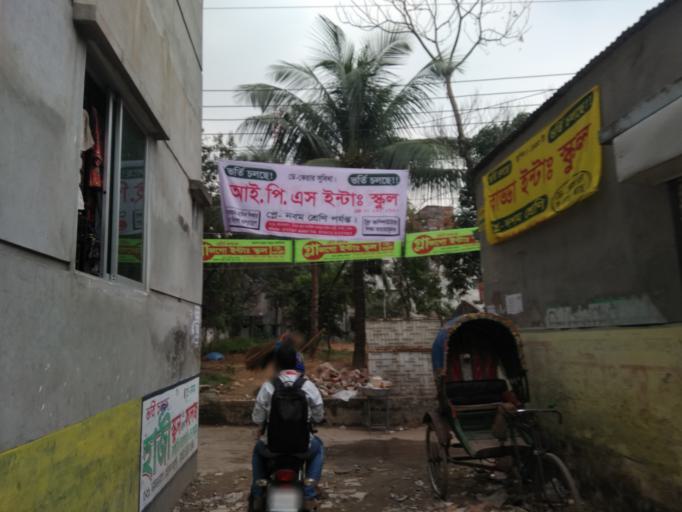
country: BD
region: Dhaka
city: Paltan
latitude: 23.7832
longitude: 90.4297
